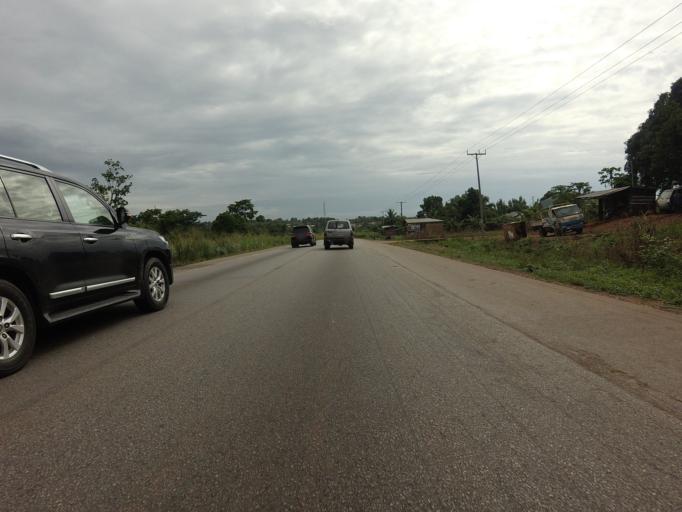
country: GH
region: Eastern
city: Nkawkaw
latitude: 6.5999
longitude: -0.8870
